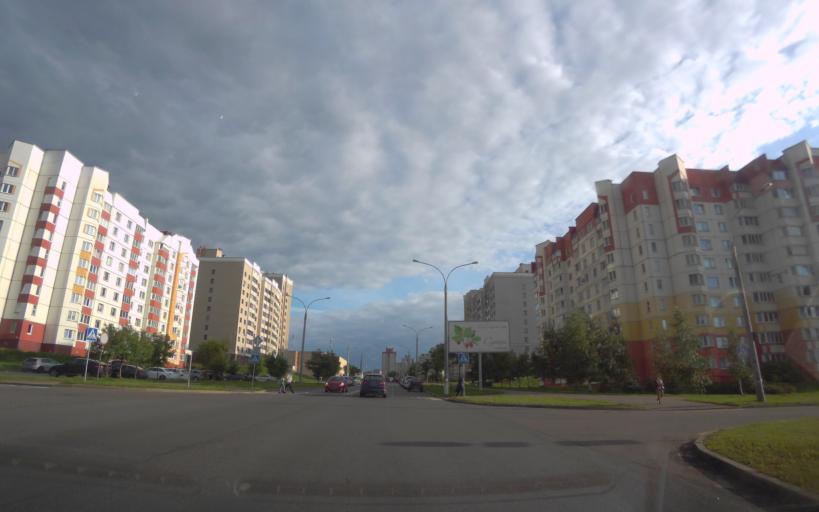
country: BY
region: Minsk
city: Zhdanovichy
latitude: 53.9201
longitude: 27.4496
